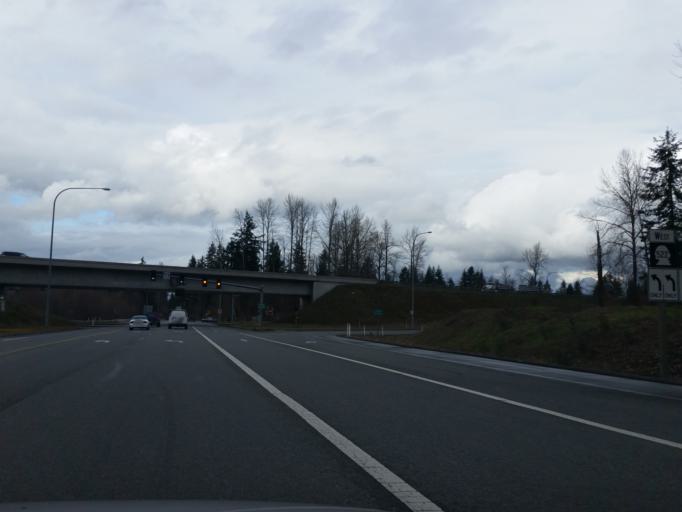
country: US
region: Washington
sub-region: Snohomish County
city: Maltby
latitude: 47.8126
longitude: -122.0770
